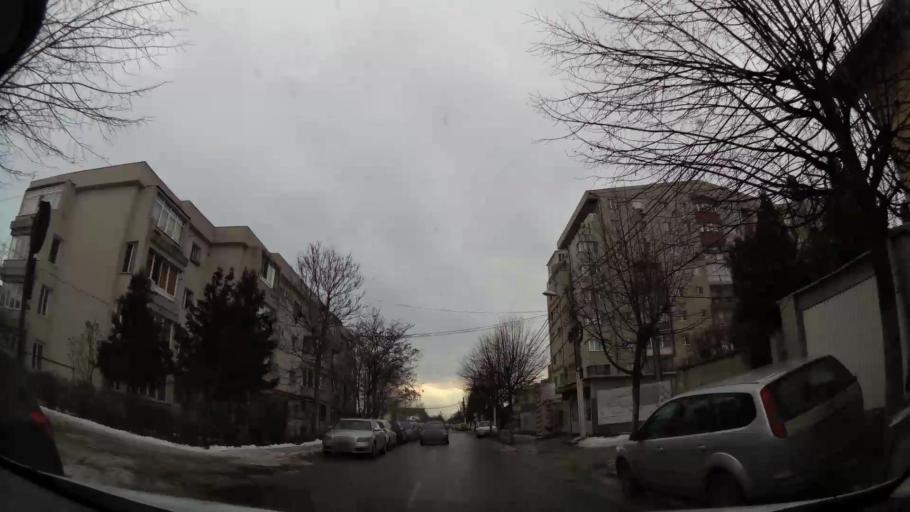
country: RO
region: Ilfov
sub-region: Voluntari City
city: Voluntari
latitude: 44.4946
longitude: 26.1880
